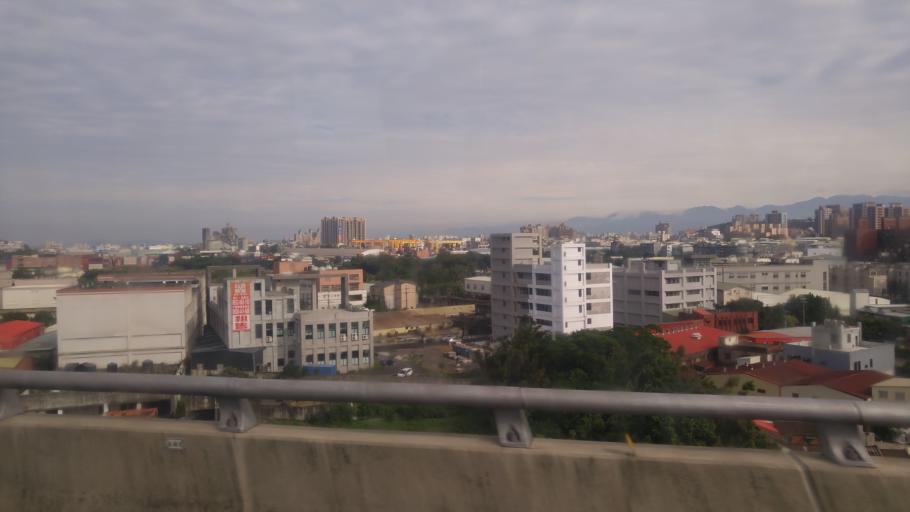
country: TW
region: Taiwan
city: Daxi
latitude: 24.9148
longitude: 121.1668
